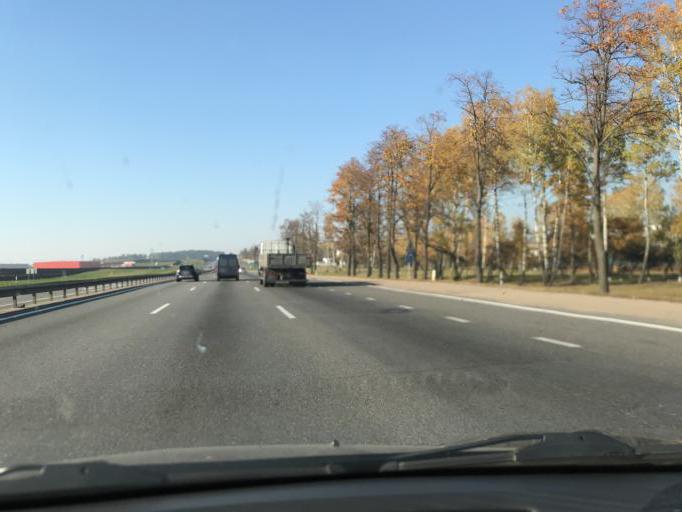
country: BY
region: Minsk
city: Pryvol'ny
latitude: 53.8074
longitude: 27.7884
